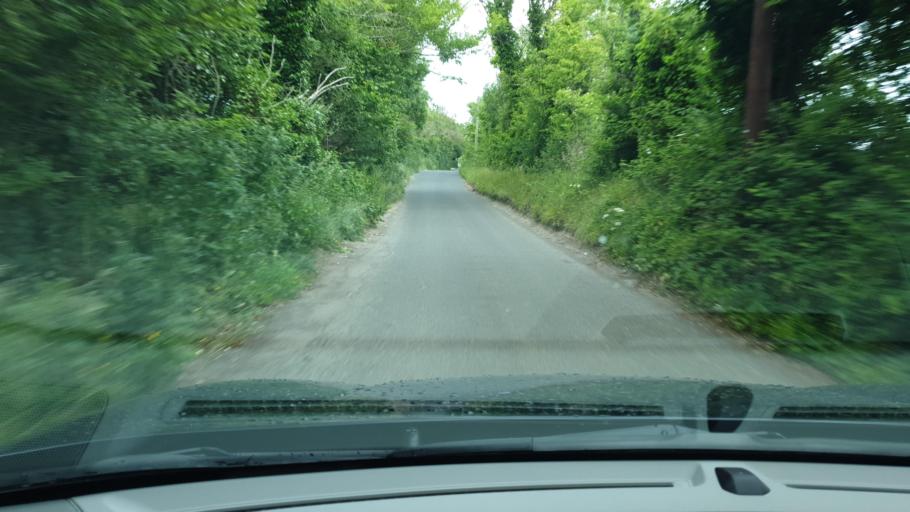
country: IE
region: Leinster
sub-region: An Mhi
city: Ashbourne
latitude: 53.5105
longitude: -6.3845
